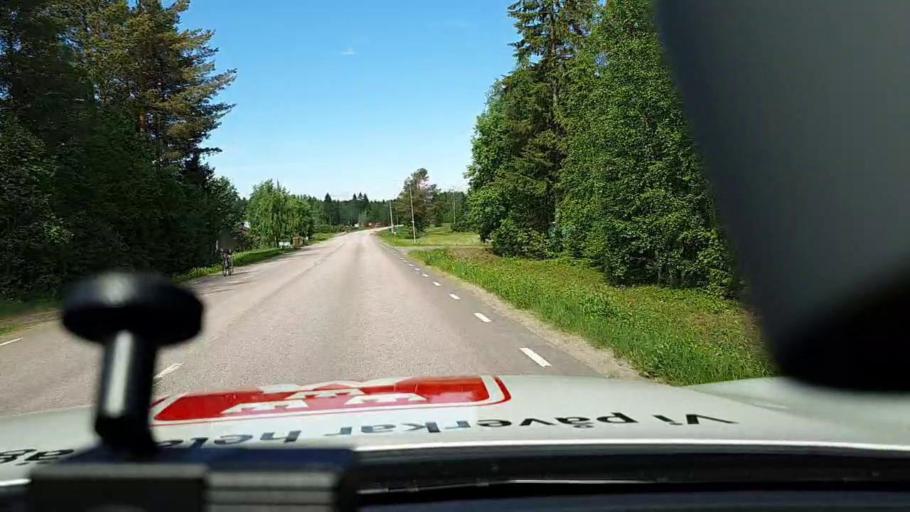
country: SE
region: Norrbotten
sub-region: Lulea Kommun
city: Sodra Sunderbyn
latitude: 65.6425
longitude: 21.8939
